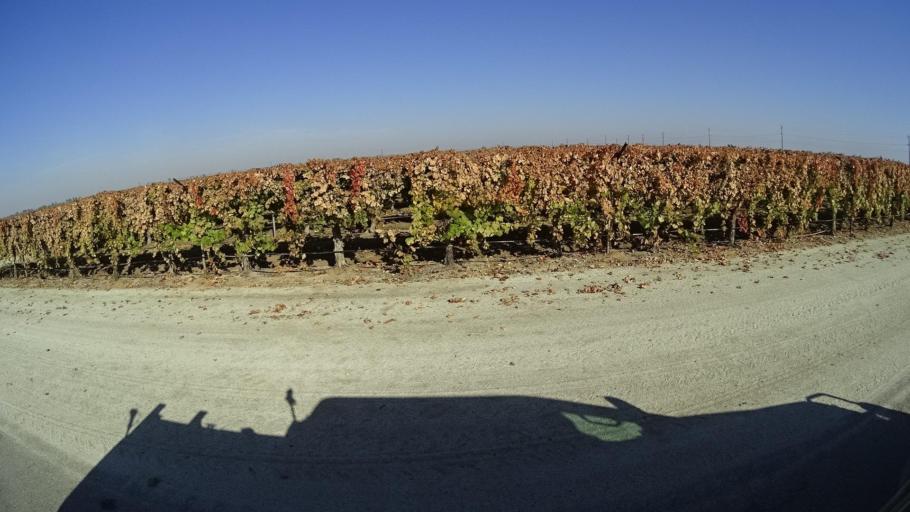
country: US
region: California
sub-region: Kern County
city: Delano
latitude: 35.7396
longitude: -119.2073
